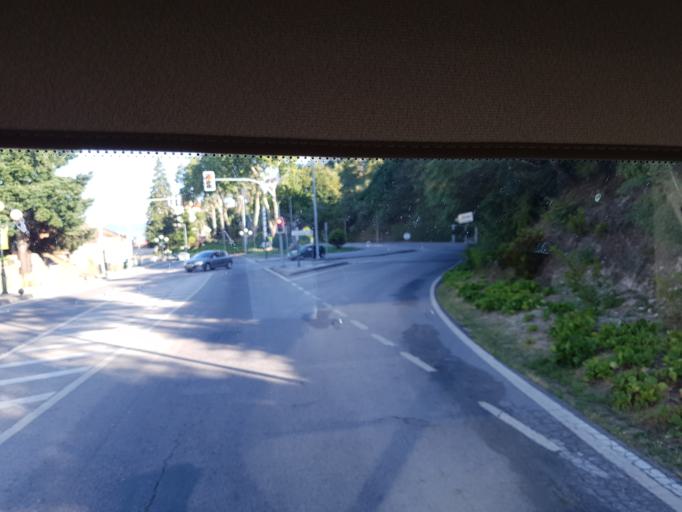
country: PT
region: Castelo Branco
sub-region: Covilha
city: Covilha
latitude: 40.2757
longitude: -7.5052
